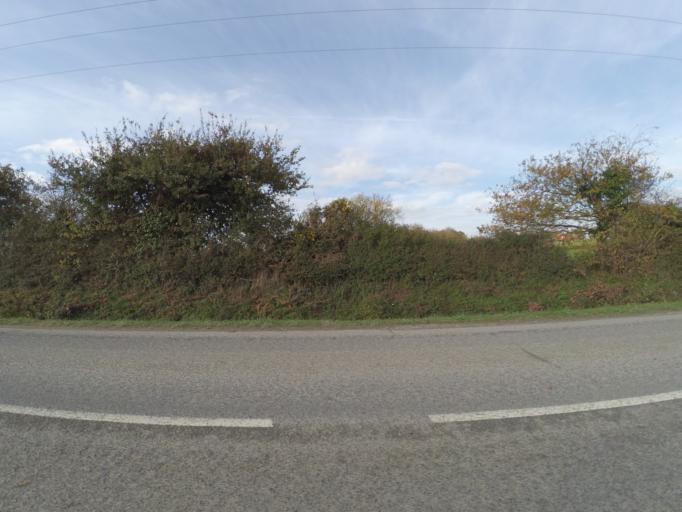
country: FR
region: Pays de la Loire
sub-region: Departement de la Vendee
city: Saint-Hilaire-de-Loulay
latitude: 47.0017
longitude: -1.3714
